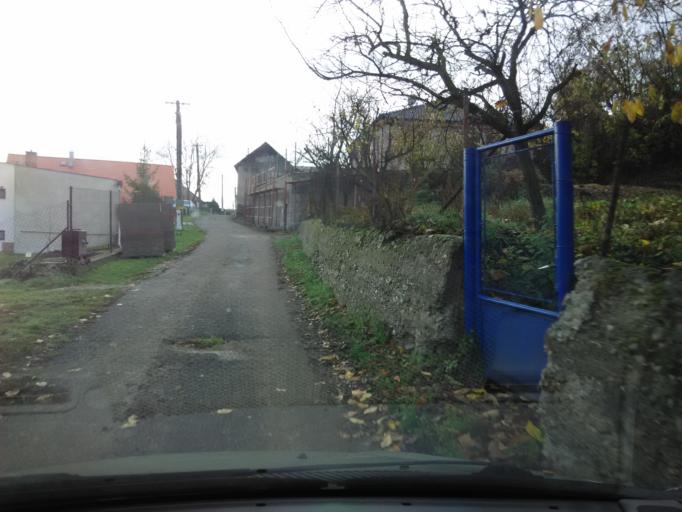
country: SK
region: Nitriansky
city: Tlmace
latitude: 48.2956
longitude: 18.5591
